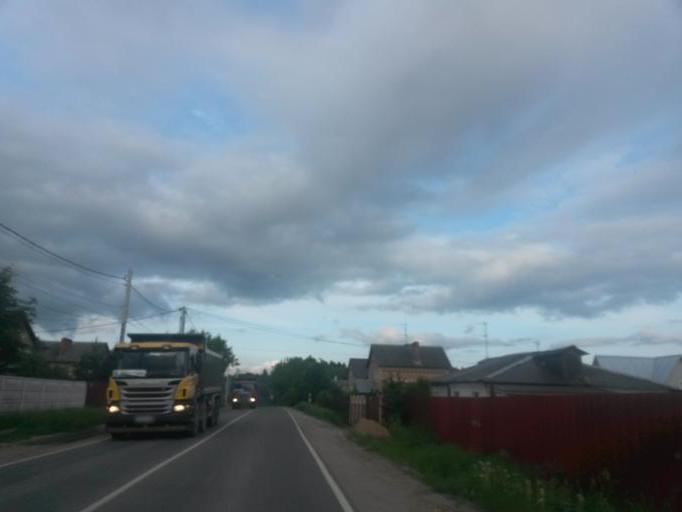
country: RU
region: Moskovskaya
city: Klimovsk
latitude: 55.3485
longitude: 37.5492
